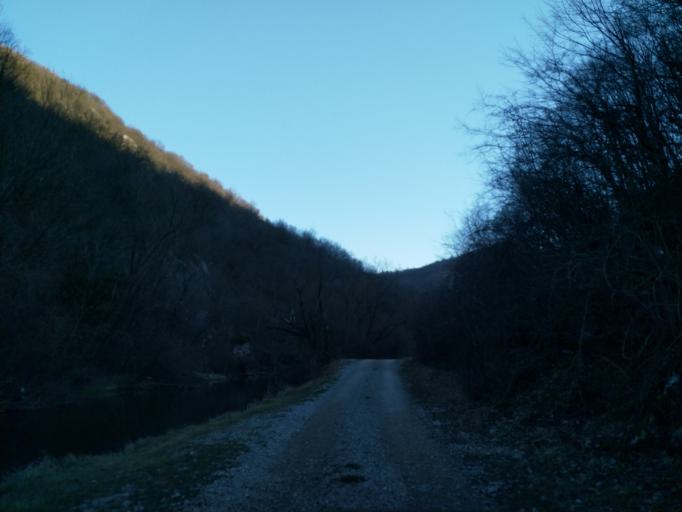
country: RS
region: Central Serbia
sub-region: Pomoravski Okrug
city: Paracin
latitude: 43.9261
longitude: 21.5252
